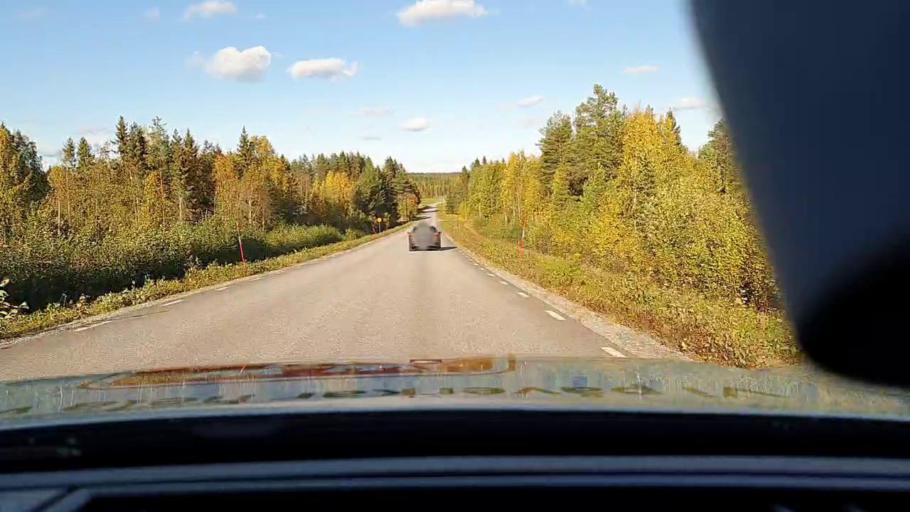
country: SE
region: Norrbotten
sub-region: Pitea Kommun
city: Norrfjarden
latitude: 65.5073
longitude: 21.4835
